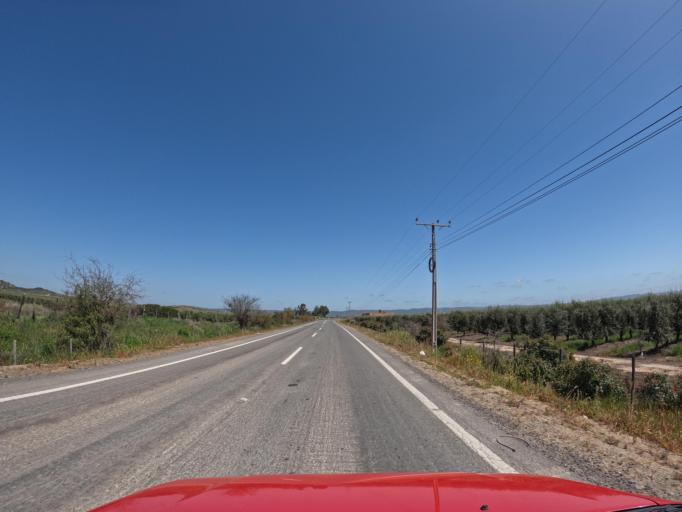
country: CL
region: O'Higgins
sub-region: Provincia de Colchagua
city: Santa Cruz
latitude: -34.7357
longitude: -71.7017
